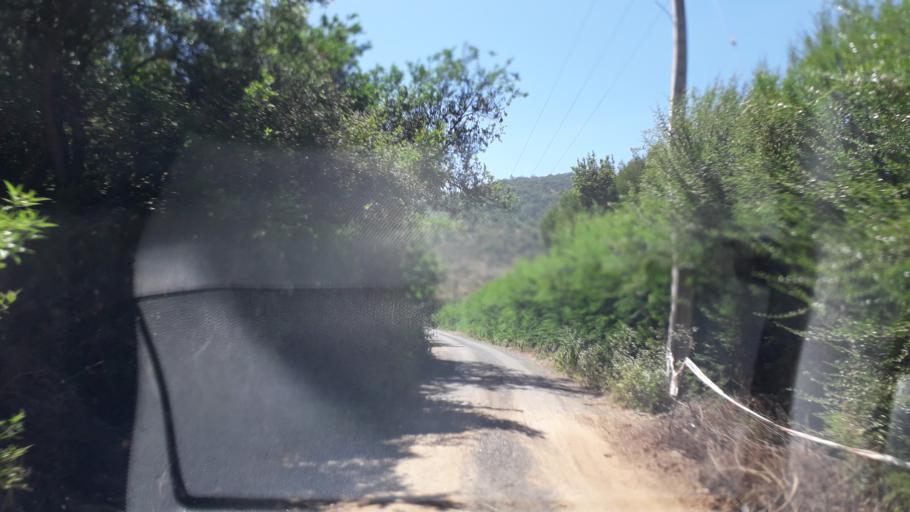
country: CL
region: Valparaiso
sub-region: Provincia de Marga Marga
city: Limache
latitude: -33.0737
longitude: -71.2153
